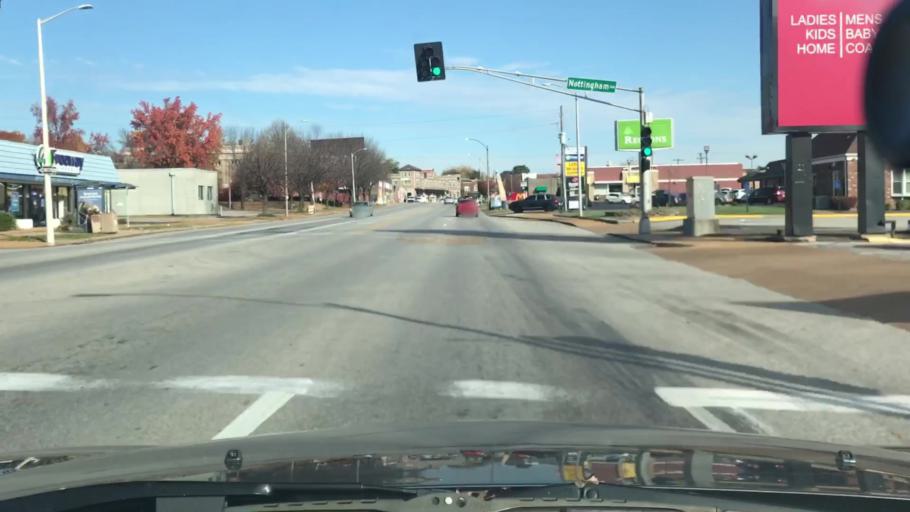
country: US
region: Missouri
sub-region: Saint Louis County
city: Lemay
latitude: 38.5850
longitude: -90.2766
